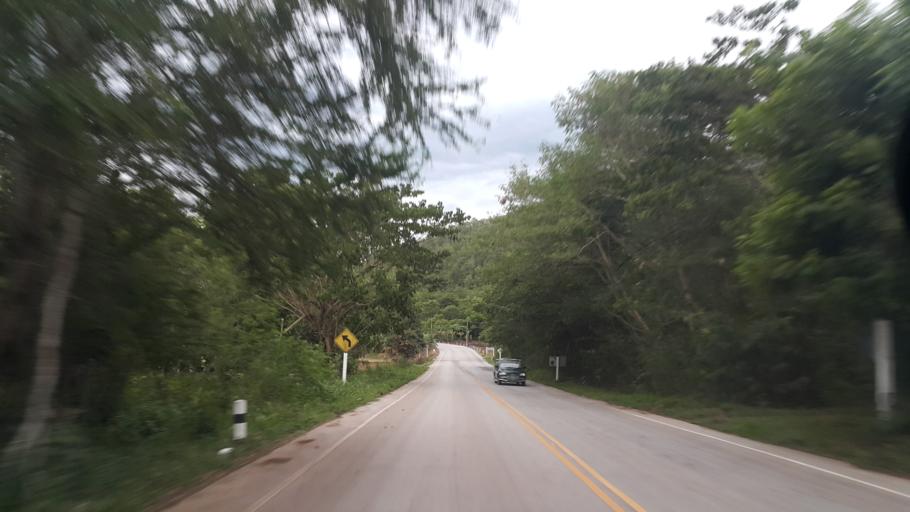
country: TH
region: Loei
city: Na Haeo
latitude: 17.4958
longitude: 101.1847
